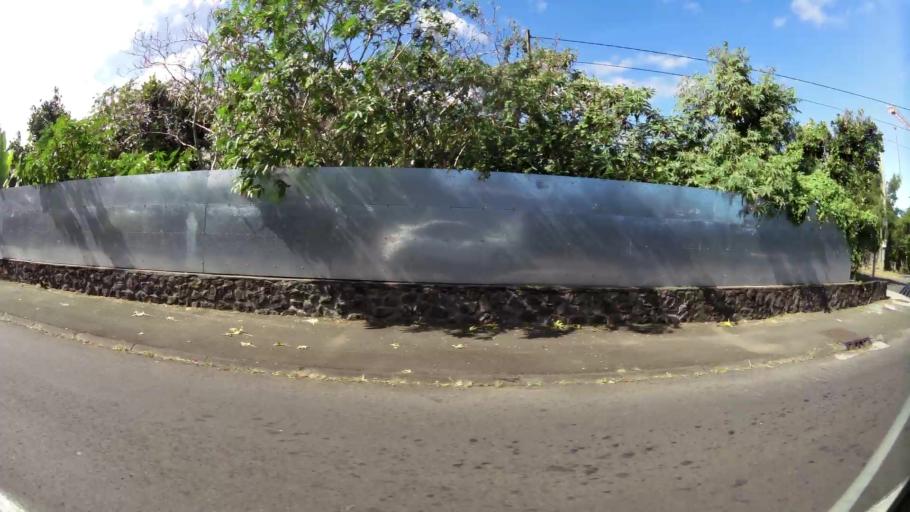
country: RE
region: Reunion
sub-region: Reunion
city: Le Tampon
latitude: -21.2926
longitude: 55.5099
